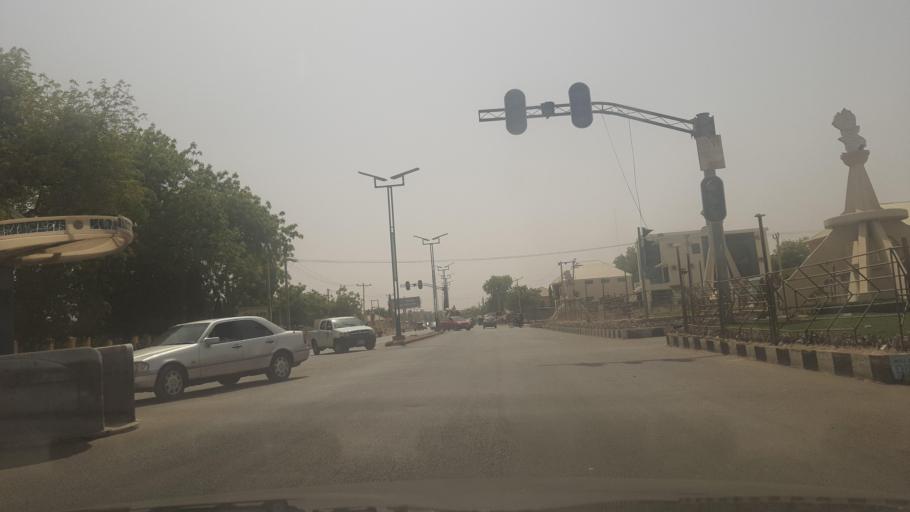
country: NG
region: Gombe
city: Gombe
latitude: 10.2861
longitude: 11.1411
